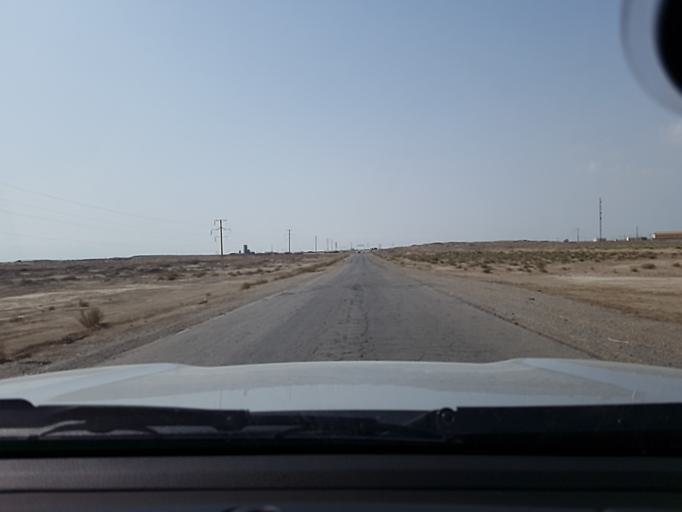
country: TM
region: Balkan
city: Gumdag
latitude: 39.1226
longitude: 54.5796
